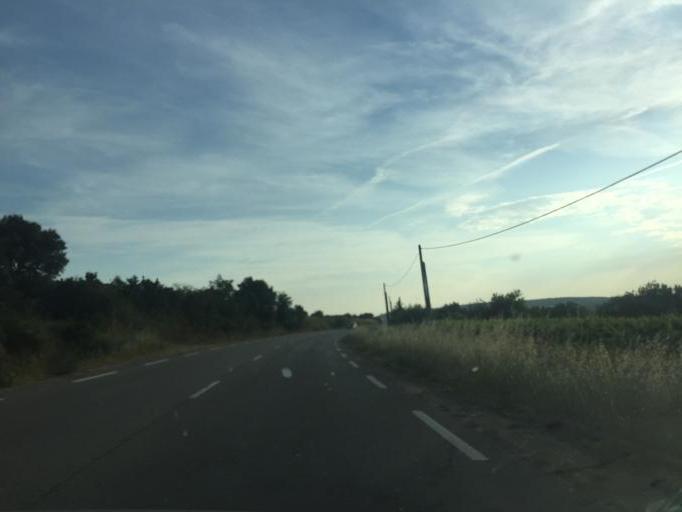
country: FR
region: Languedoc-Roussillon
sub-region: Departement du Gard
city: Roquemaure
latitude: 44.0286
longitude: 4.7567
